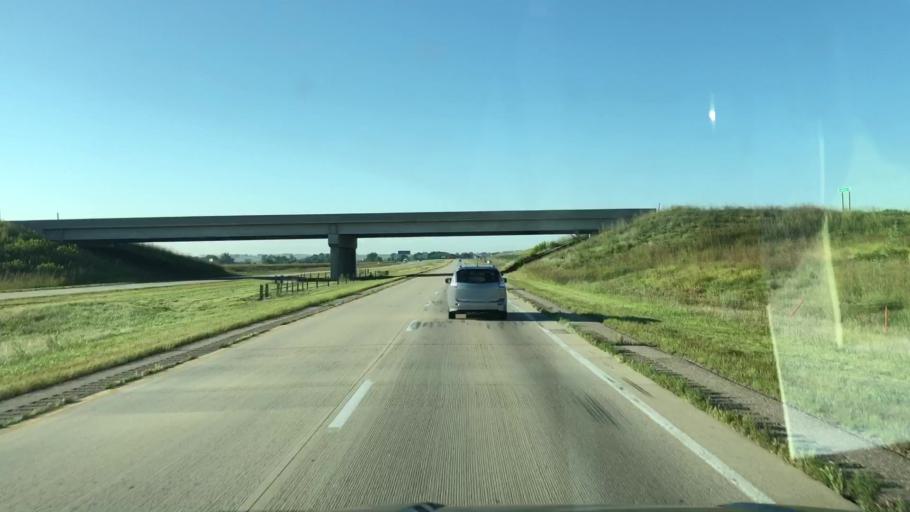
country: US
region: Iowa
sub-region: Plymouth County
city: Le Mars
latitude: 42.7651
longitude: -96.2095
